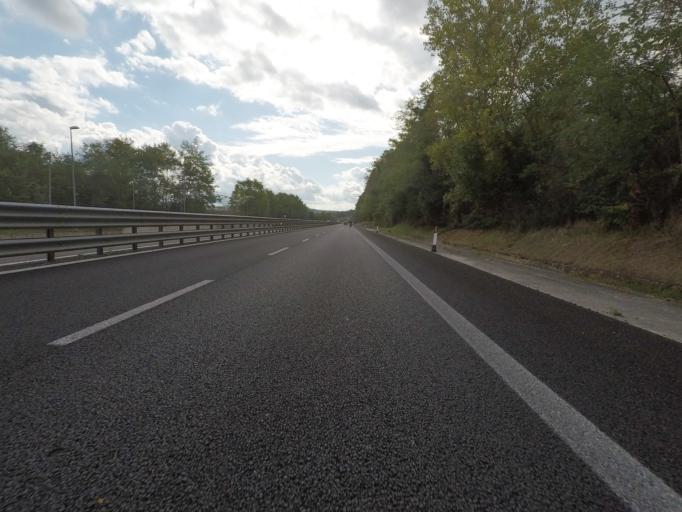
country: IT
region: Tuscany
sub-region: Provincia di Siena
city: Serre di Rapolano
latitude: 43.2626
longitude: 11.6302
